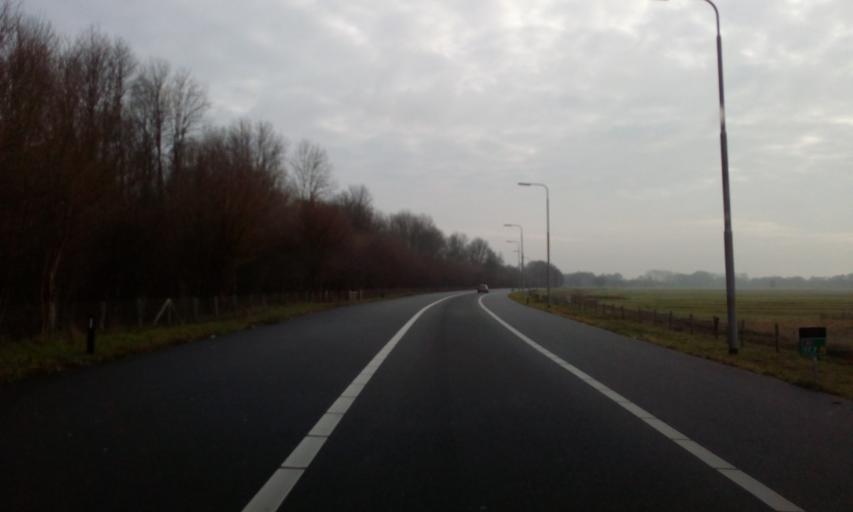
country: NL
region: North Holland
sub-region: Gemeente Naarden
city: Naarden
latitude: 52.3046
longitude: 5.1353
